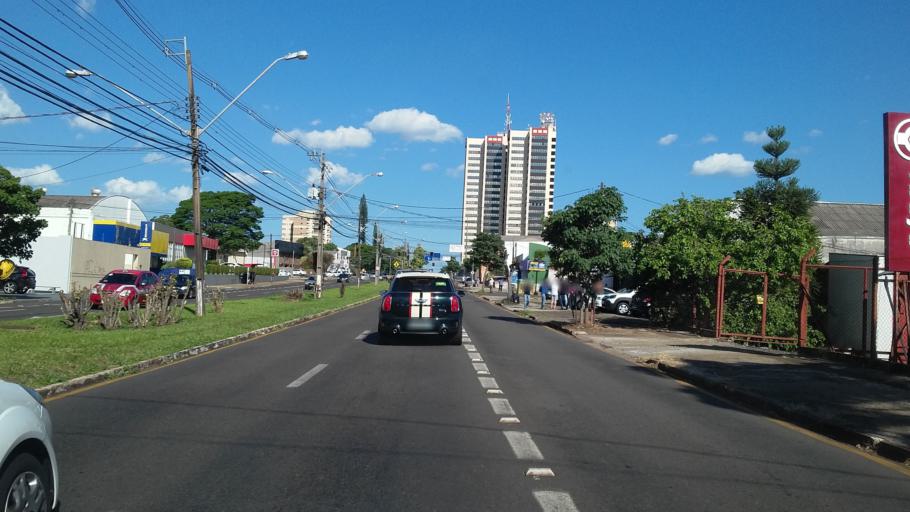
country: BR
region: Parana
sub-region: Londrina
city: Londrina
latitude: -23.3010
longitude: -51.1823
